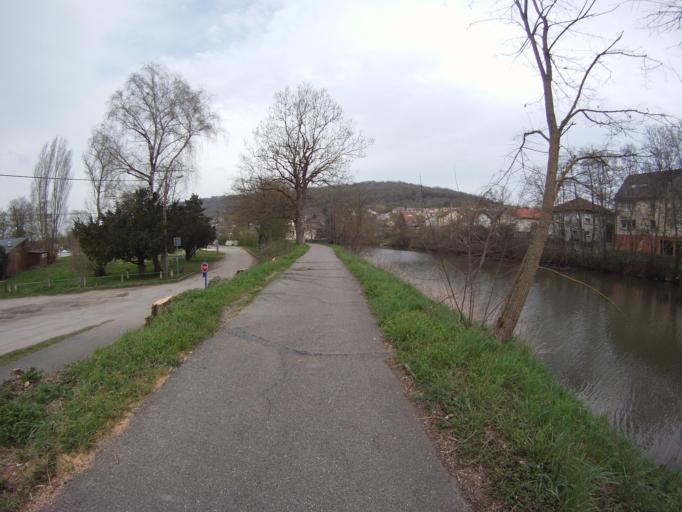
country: FR
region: Lorraine
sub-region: Departement de Meurthe-et-Moselle
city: Messein
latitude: 48.6078
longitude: 6.1491
